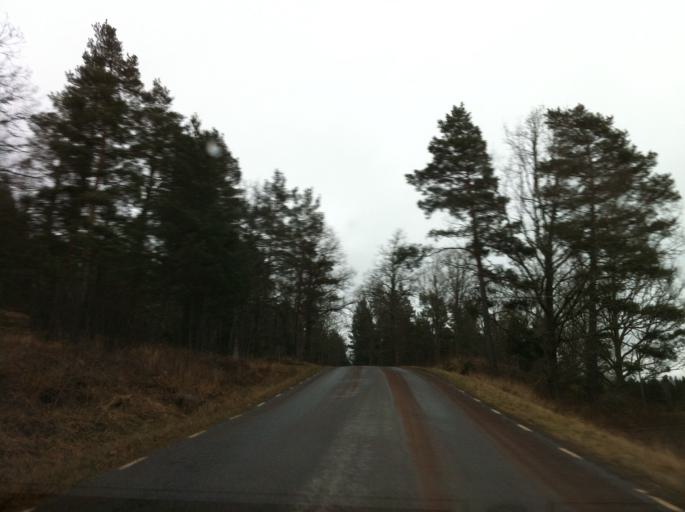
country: SE
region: Kalmar
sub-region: Vasterviks Kommun
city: Forserum
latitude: 57.9285
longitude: 16.5282
